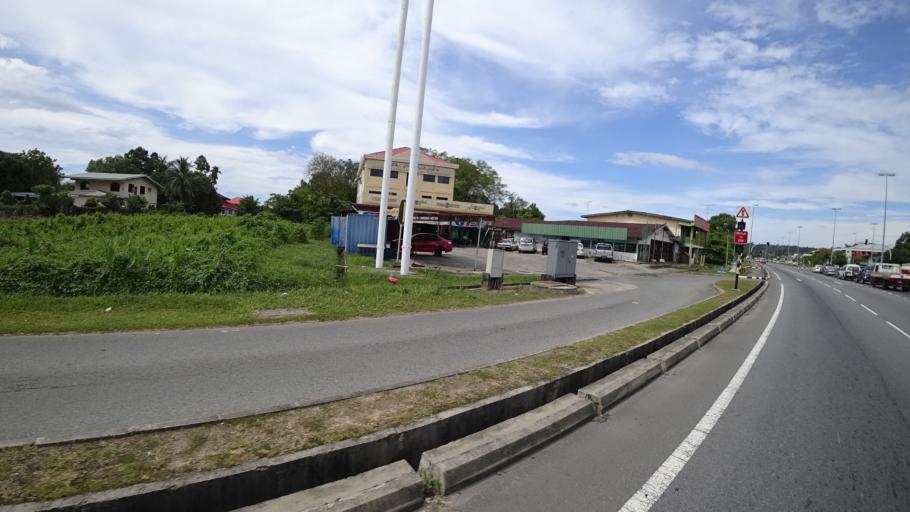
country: BN
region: Brunei and Muara
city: Bandar Seri Begawan
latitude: 4.8889
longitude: 114.8439
